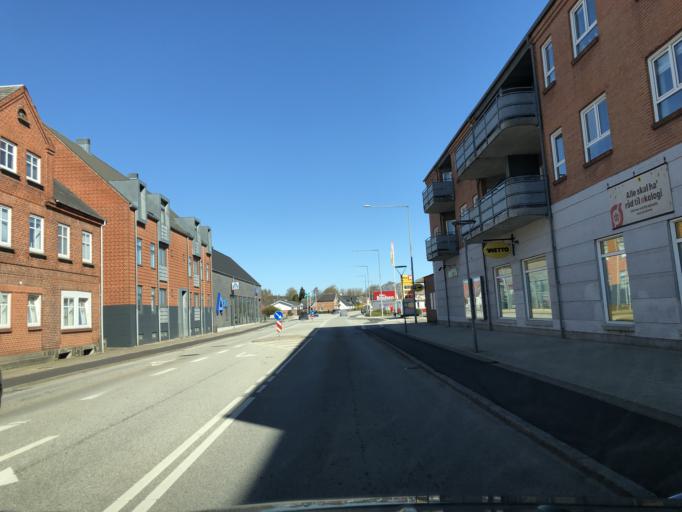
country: DK
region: North Denmark
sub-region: Rebild Kommune
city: Stovring
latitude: 56.8921
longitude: 9.8370
